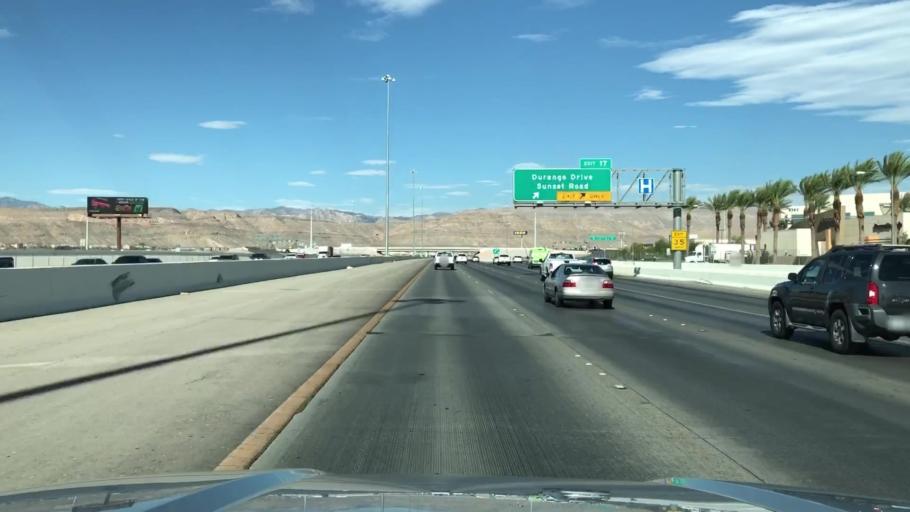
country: US
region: Nevada
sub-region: Clark County
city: Spring Valley
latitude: 36.0665
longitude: -115.2718
